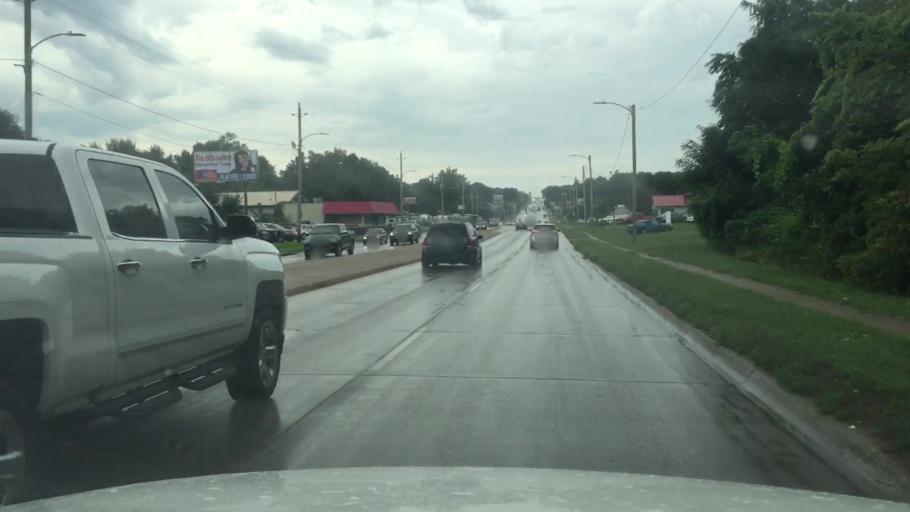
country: US
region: Iowa
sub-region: Polk County
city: Des Moines
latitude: 41.5734
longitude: -93.5970
